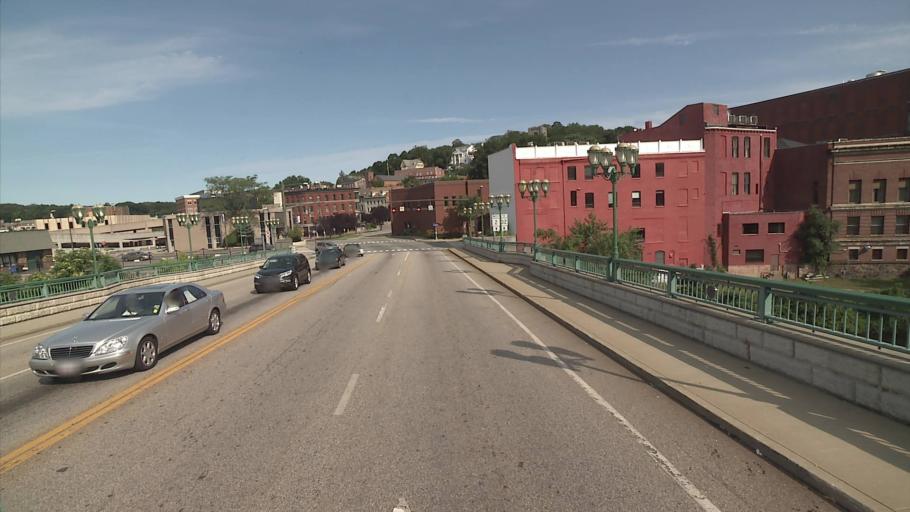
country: US
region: Connecticut
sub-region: New London County
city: Norwich
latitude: 41.5233
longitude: -72.0758
